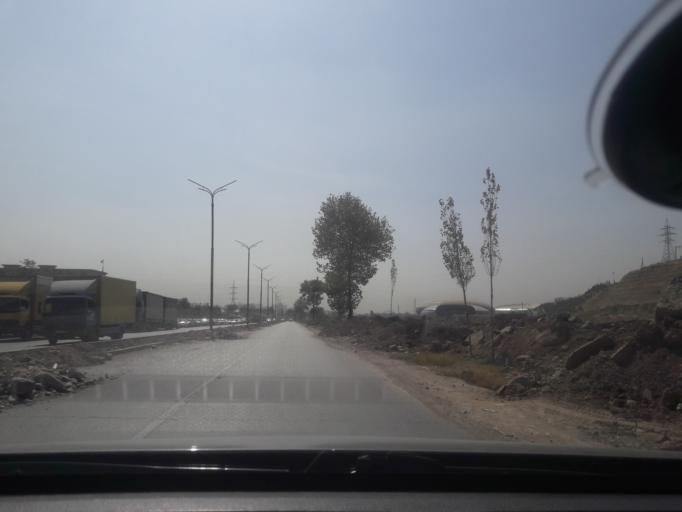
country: TJ
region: Dushanbe
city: Dushanbe
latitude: 38.6081
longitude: 68.7715
